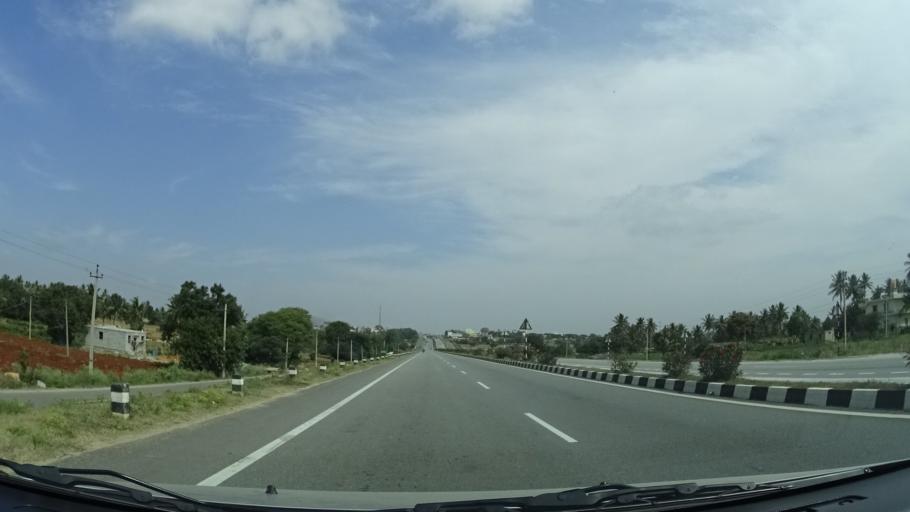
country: IN
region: Karnataka
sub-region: Chikkaballapur
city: Gudibanda
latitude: 13.5775
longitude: 77.7815
